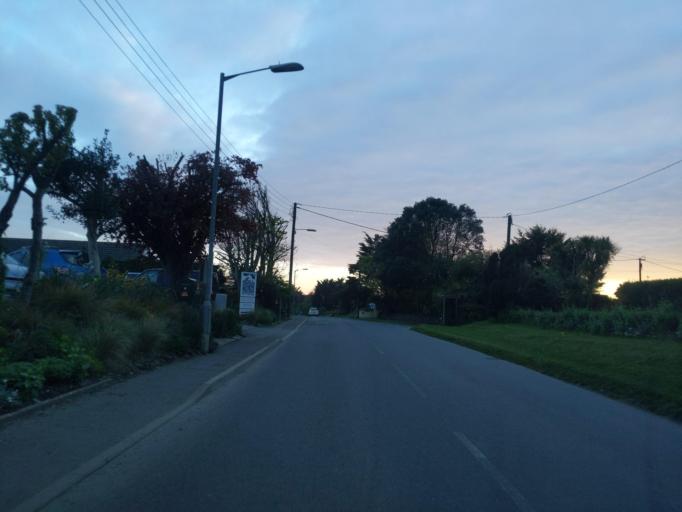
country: GB
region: England
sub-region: Cornwall
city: Polzeath
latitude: 50.5539
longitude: -4.8940
